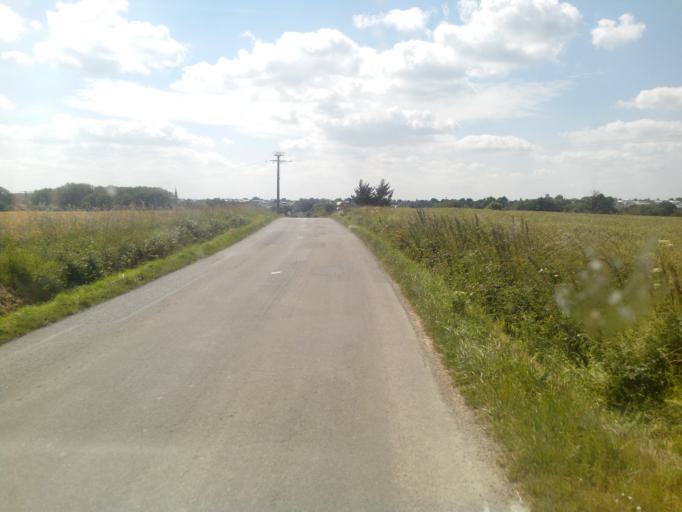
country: FR
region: Brittany
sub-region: Departement d'Ille-et-Vilaine
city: Acigne
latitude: 48.1318
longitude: -1.5168
